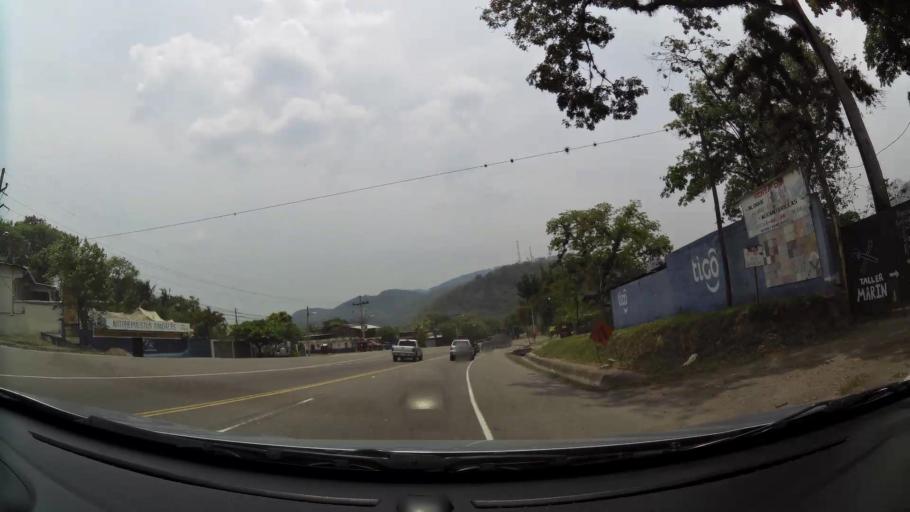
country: HN
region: Comayagua
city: Taulabe
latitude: 14.6961
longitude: -87.9621
